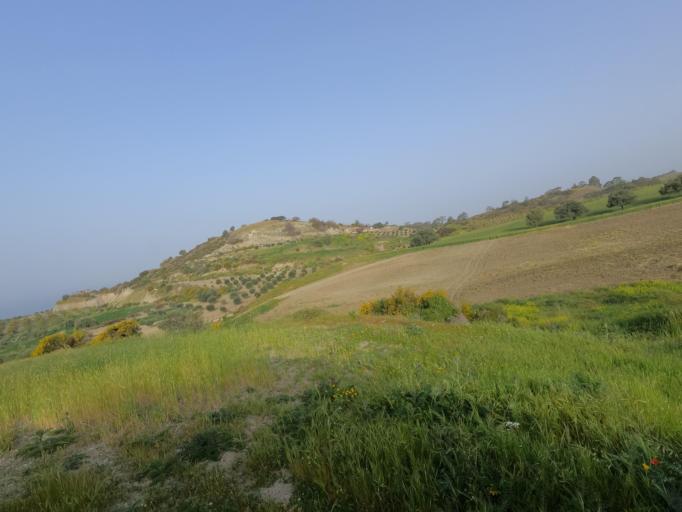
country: CY
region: Pafos
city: Polis
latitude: 34.9855
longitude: 32.3332
